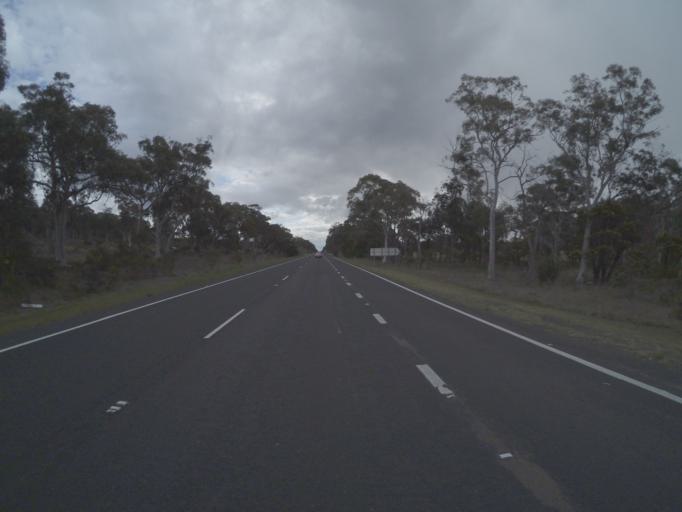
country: AU
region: New South Wales
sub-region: Goulburn Mulwaree
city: Goulburn
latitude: -34.7440
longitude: 149.8865
